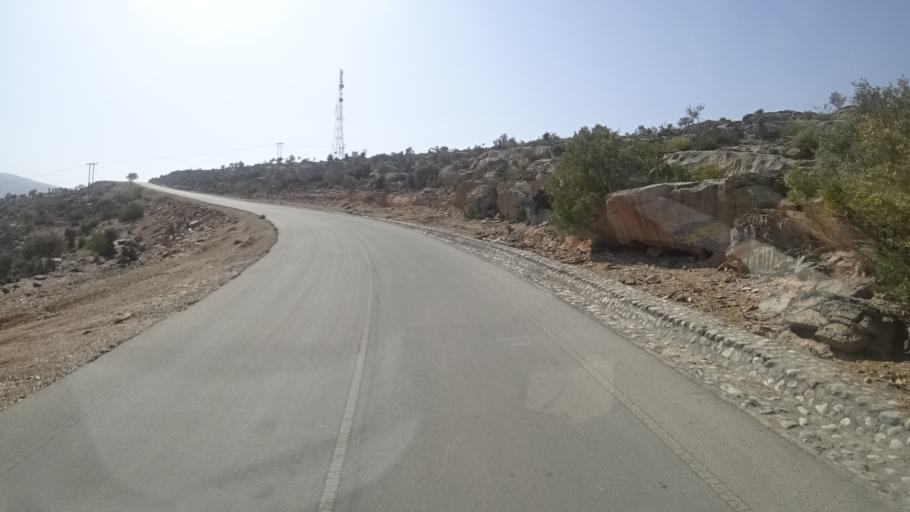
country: OM
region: Muhafazat ad Dakhiliyah
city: Bahla'
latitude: 23.2146
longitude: 57.2006
